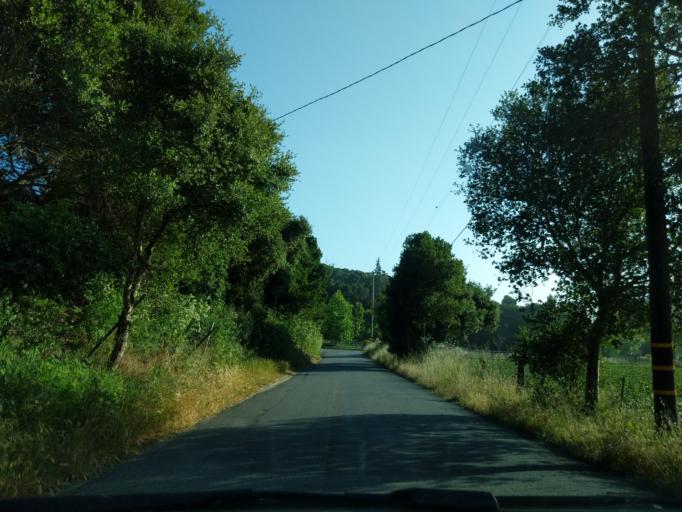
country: US
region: California
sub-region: Monterey County
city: Las Lomas
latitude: 36.8853
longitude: -121.7258
